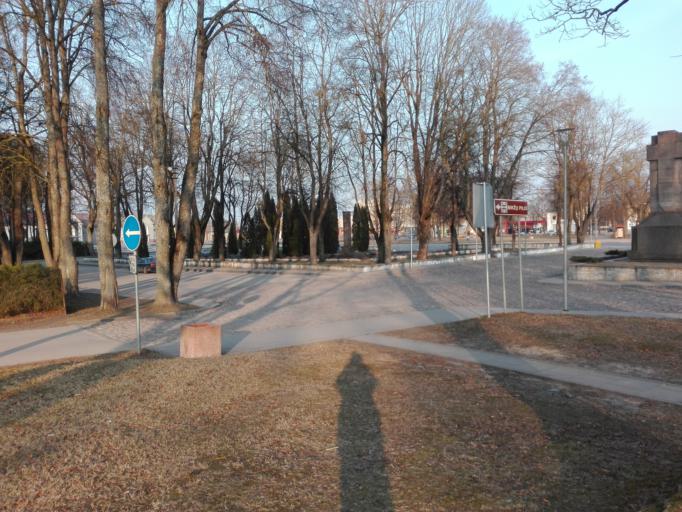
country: LT
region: Panevezys
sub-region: Birzai
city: Birzai
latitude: 56.2042
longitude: 24.7577
